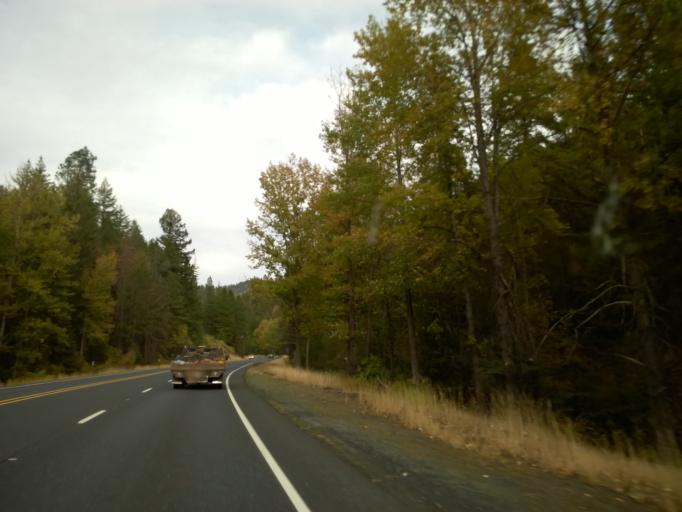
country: US
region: Washington
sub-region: Chelan County
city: Leavenworth
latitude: 47.3951
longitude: -120.6319
